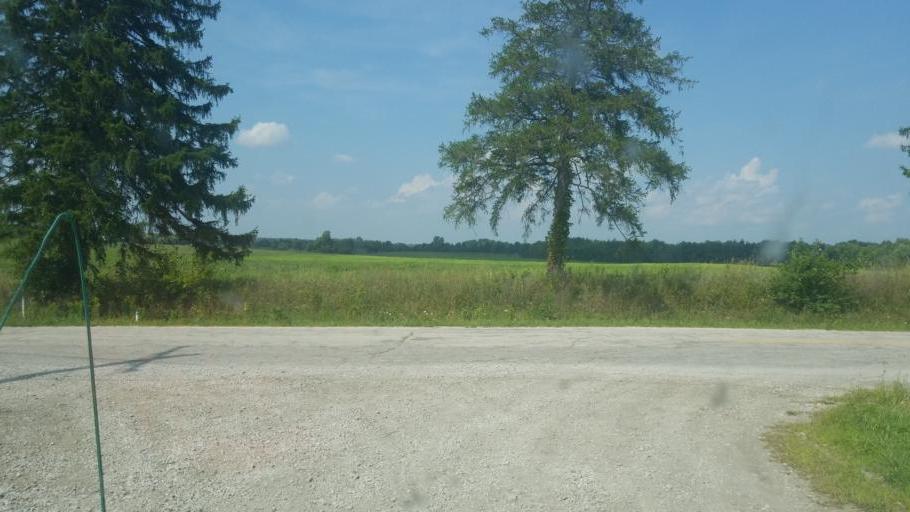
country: US
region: Ohio
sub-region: Huron County
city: New London
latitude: 41.0654
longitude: -82.4102
